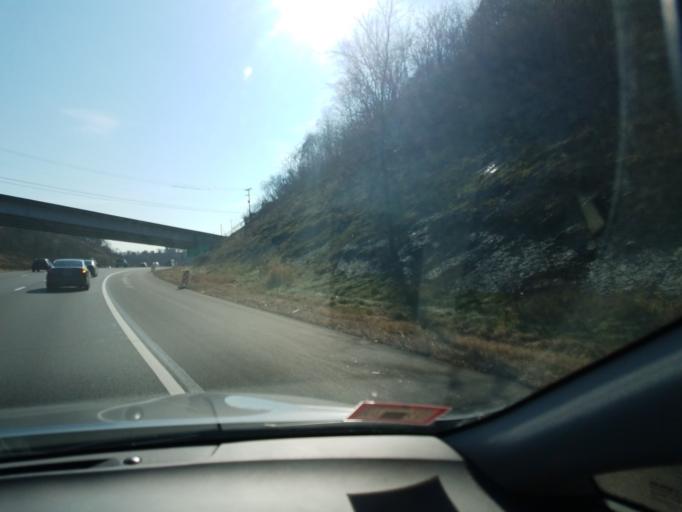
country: US
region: Pennsylvania
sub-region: Allegheny County
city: West View
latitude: 40.5179
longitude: -80.0538
